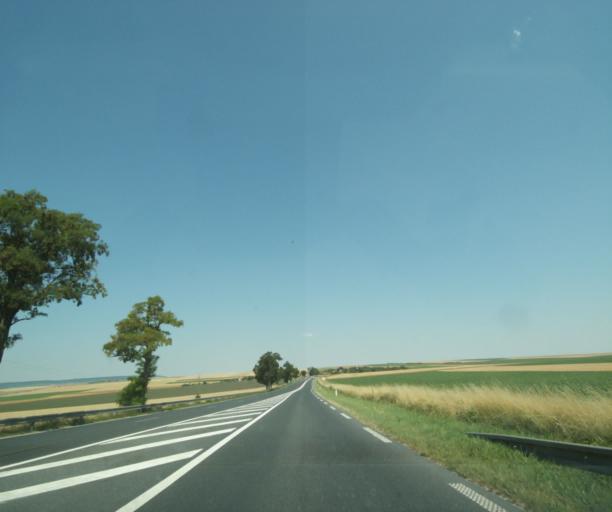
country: FR
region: Champagne-Ardenne
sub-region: Departement de la Marne
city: Fagnieres
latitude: 49.0563
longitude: 4.2998
